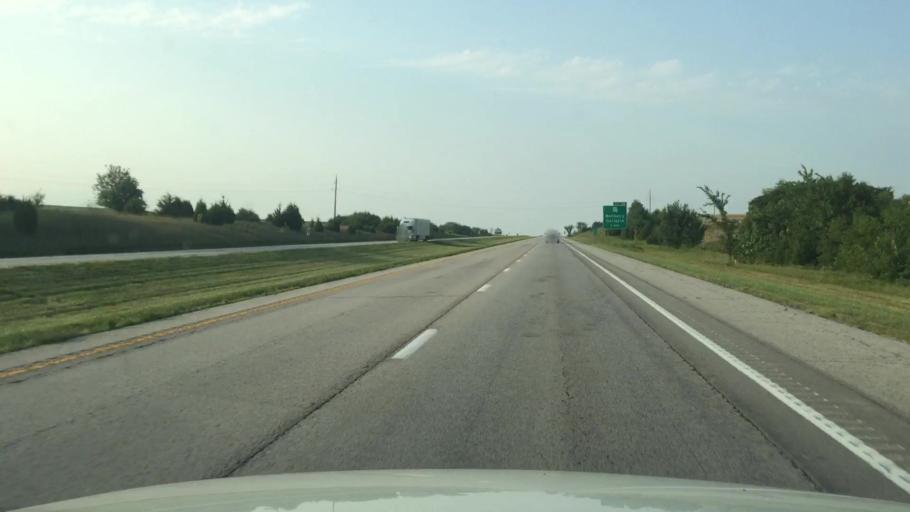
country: US
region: Missouri
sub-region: Harrison County
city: Bethany
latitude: 40.1915
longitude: -94.0142
